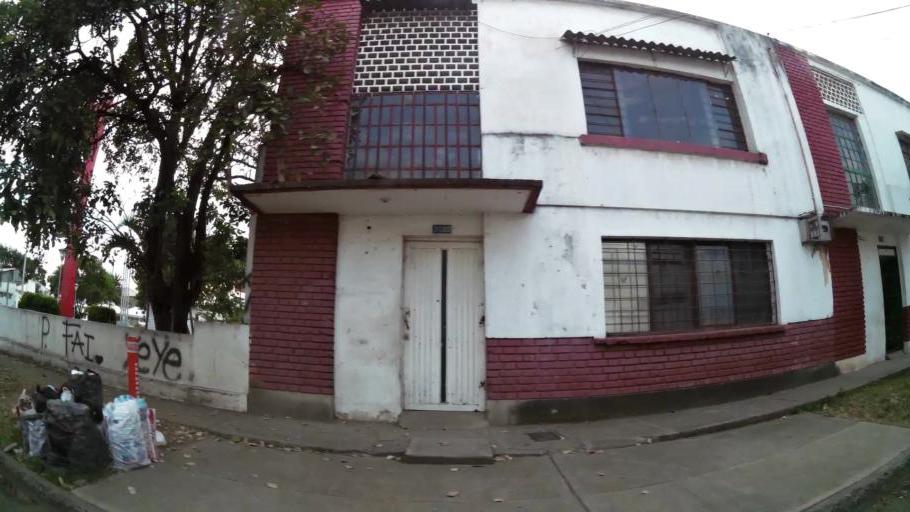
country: CO
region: Valle del Cauca
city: Cali
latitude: 3.4545
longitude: -76.5130
